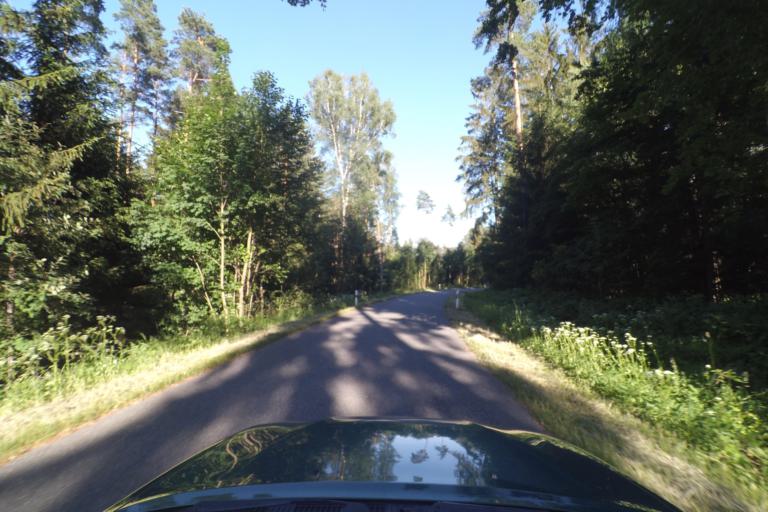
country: DE
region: Bavaria
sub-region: Upper Palatinate
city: Speinshart
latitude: 49.7940
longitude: 11.8228
